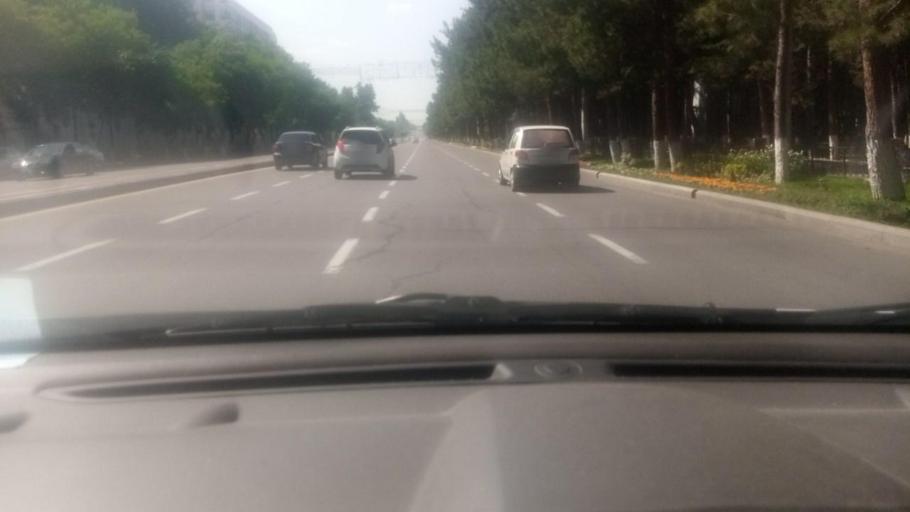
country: UZ
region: Toshkent
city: Salor
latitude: 41.3236
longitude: 69.3639
